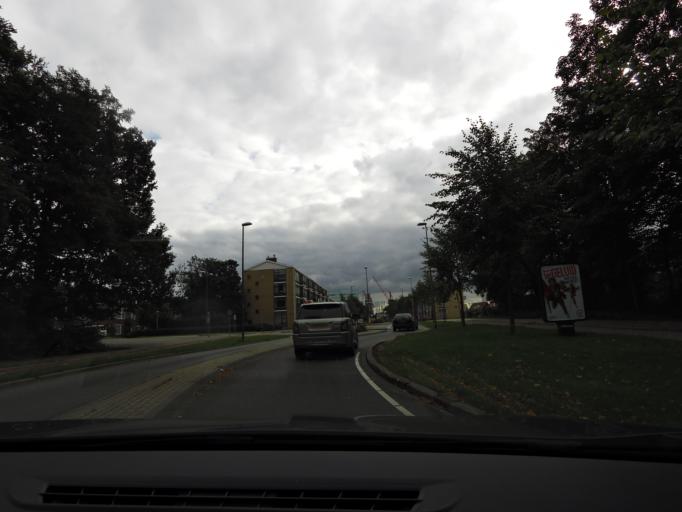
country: NL
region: South Holland
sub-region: Gemeente Schiedam
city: Schiedam
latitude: 51.9141
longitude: 4.3787
